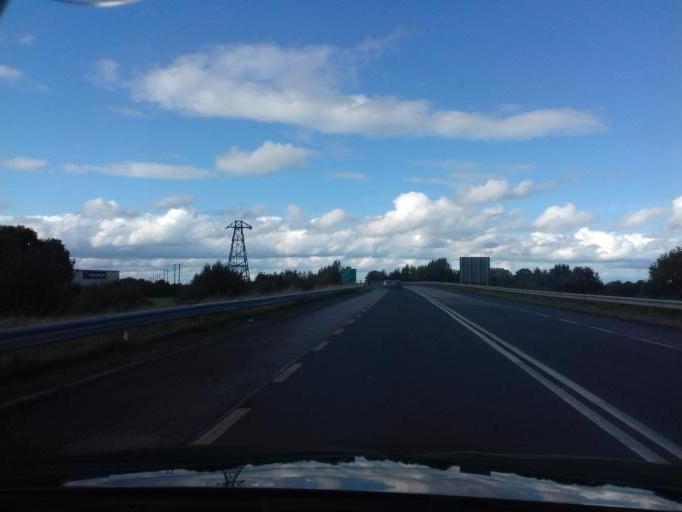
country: IE
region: Leinster
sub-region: Uibh Fhaili
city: Tullamore
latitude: 53.2671
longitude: -7.4627
